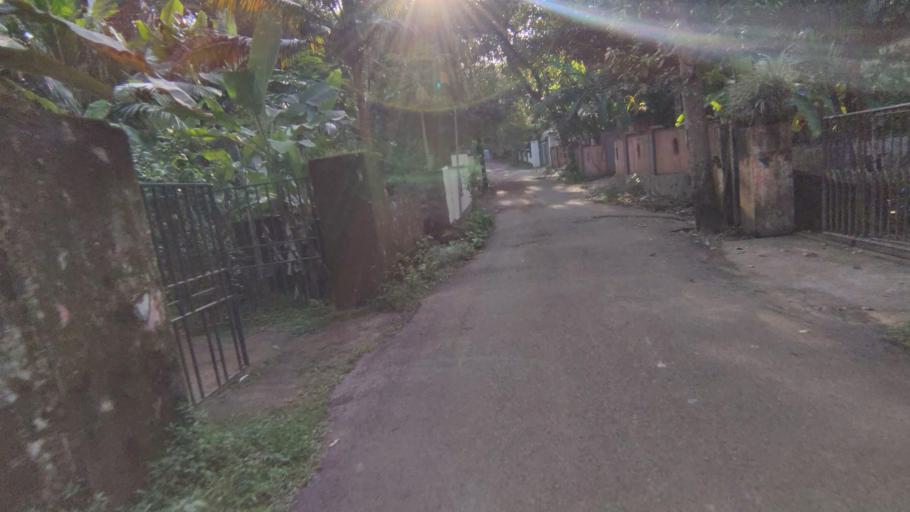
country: IN
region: Kerala
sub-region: Kottayam
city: Kottayam
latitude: 9.5974
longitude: 76.4837
